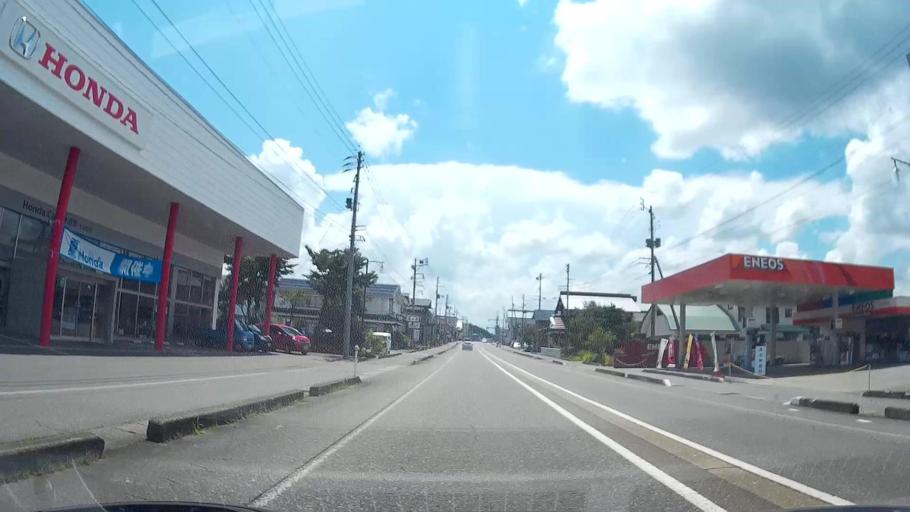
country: JP
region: Niigata
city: Tokamachi
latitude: 37.0995
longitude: 138.7343
